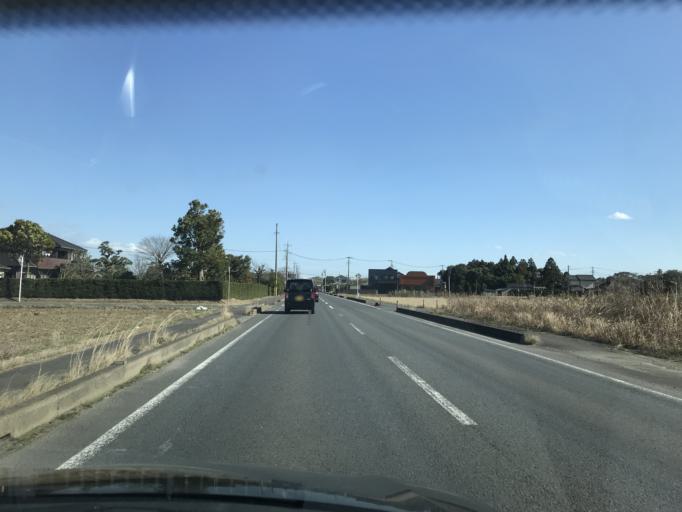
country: JP
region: Chiba
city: Omigawa
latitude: 35.8708
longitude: 140.6485
